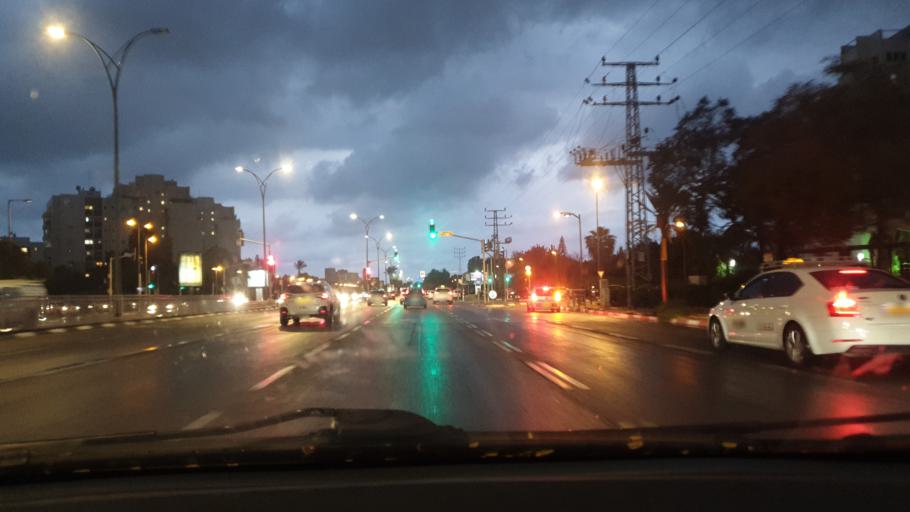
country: IL
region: Central District
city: Rishon LeZiyyon
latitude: 31.9798
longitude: 34.7797
